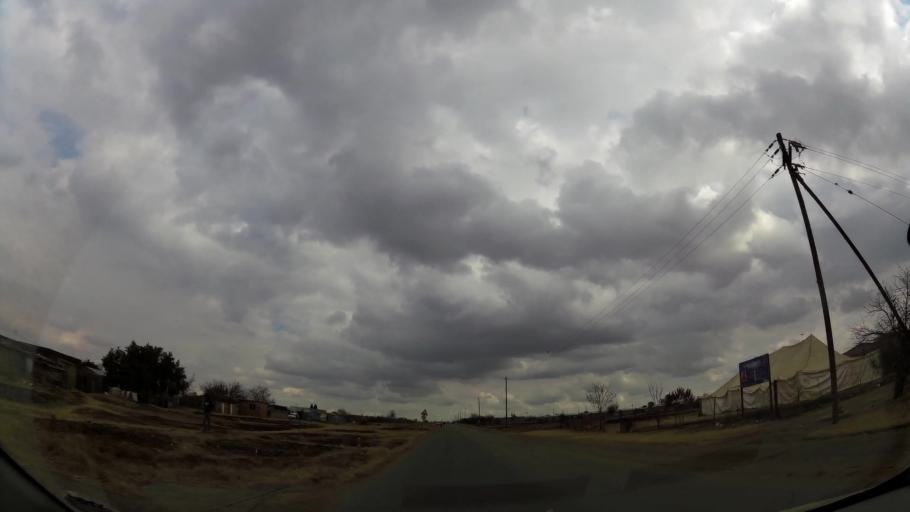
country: ZA
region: Orange Free State
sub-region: Fezile Dabi District Municipality
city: Sasolburg
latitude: -26.8494
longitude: 27.8750
